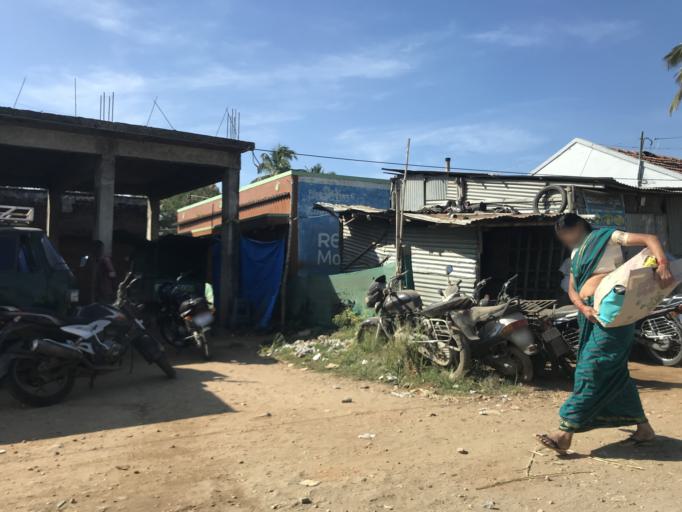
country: IN
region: Karnataka
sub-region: Mysore
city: Heggadadevankote
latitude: 12.1217
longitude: 76.4698
